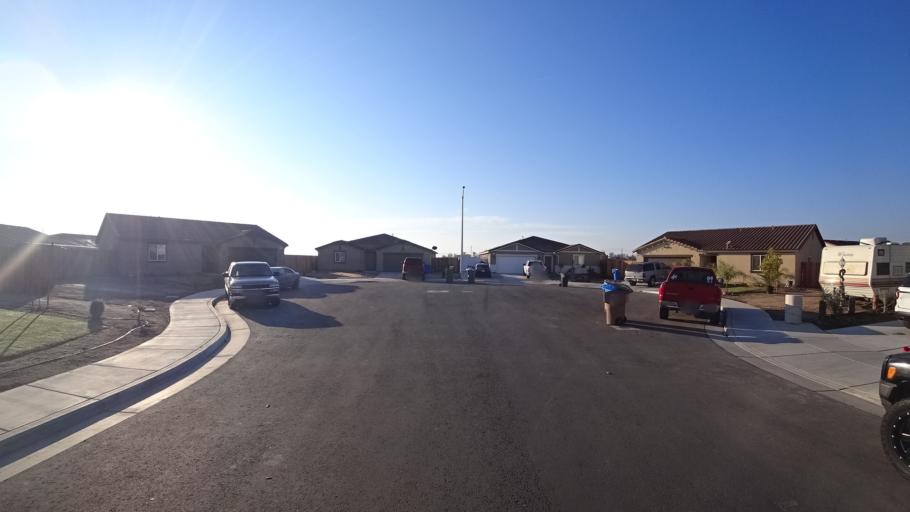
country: US
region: California
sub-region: Kern County
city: Greenfield
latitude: 35.2839
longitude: -118.9994
